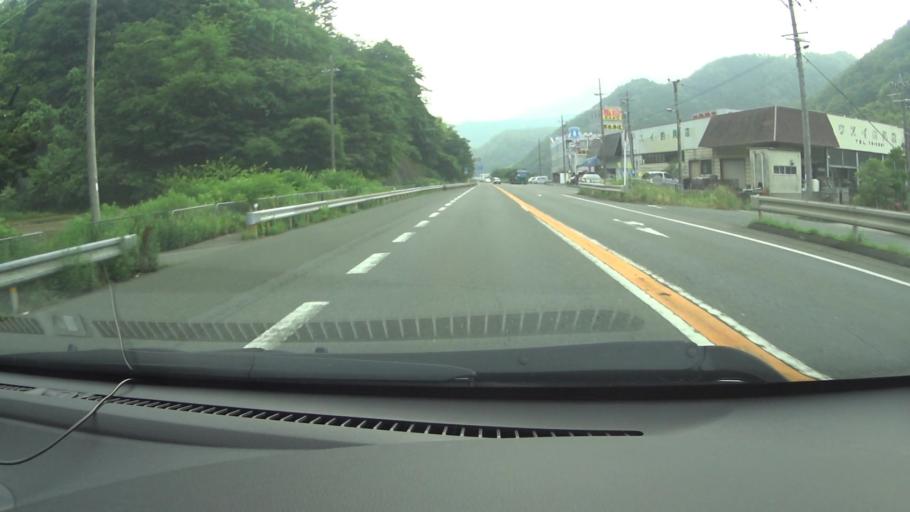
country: JP
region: Kyoto
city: Maizuru
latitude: 35.4113
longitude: 135.3305
